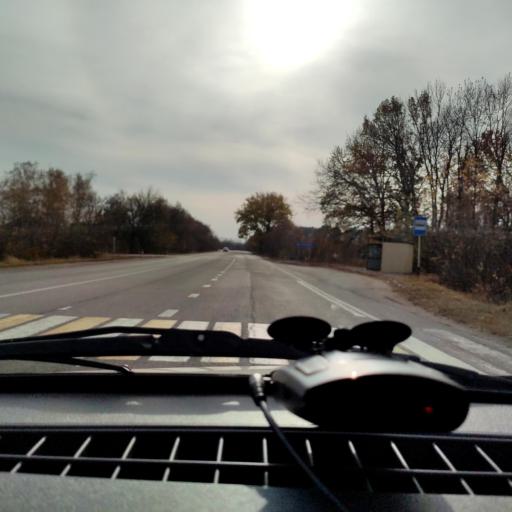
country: RU
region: Voronezj
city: Devitsa
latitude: 51.6015
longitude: 38.9718
